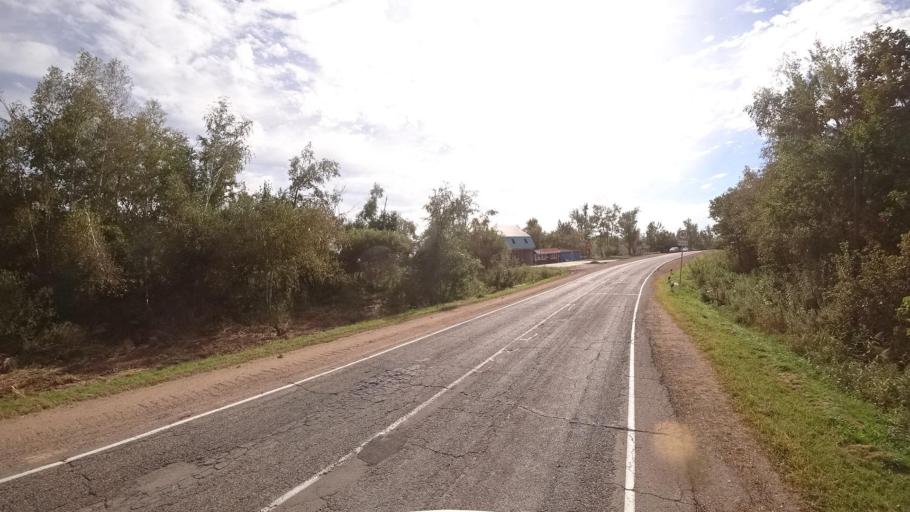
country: RU
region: Primorskiy
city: Dostoyevka
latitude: 44.3223
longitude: 133.4852
